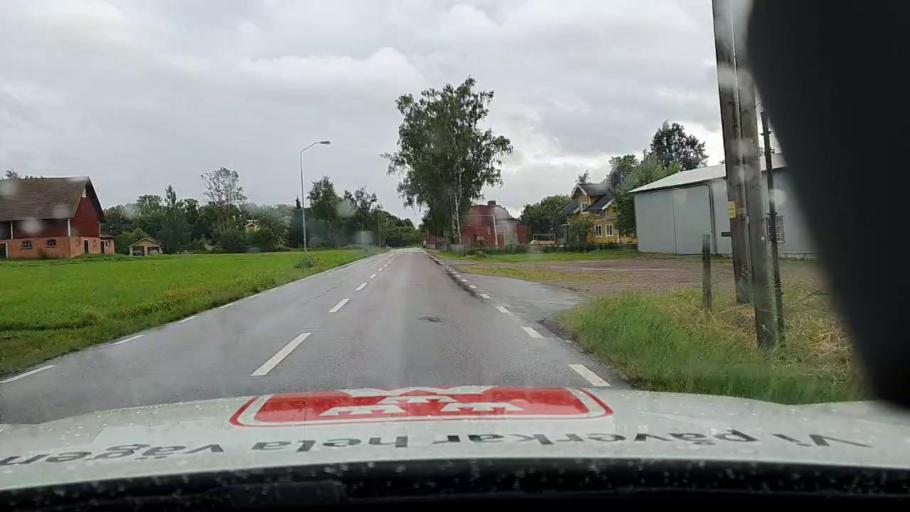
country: SE
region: Vaestra Goetaland
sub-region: Toreboda Kommun
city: Toereboda
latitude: 58.5821
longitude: 14.0050
